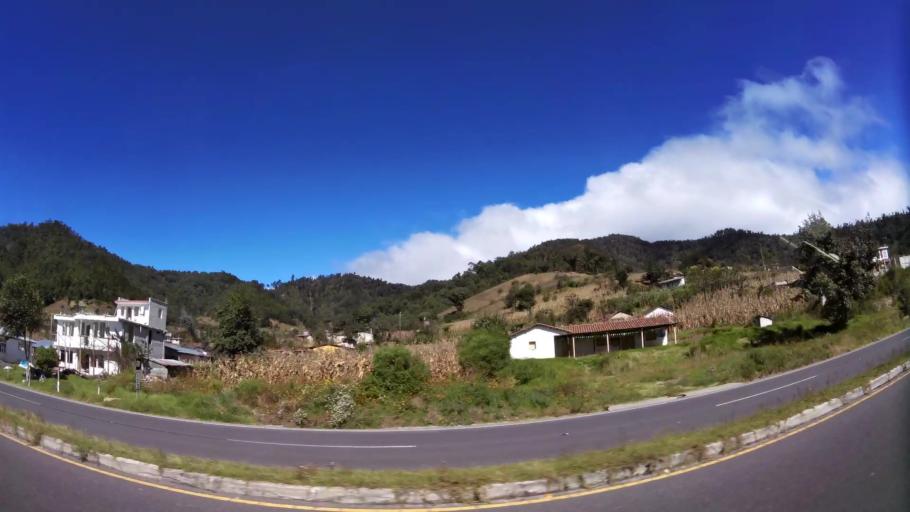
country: GT
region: Solola
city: Solola
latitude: 14.8255
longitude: -91.1968
